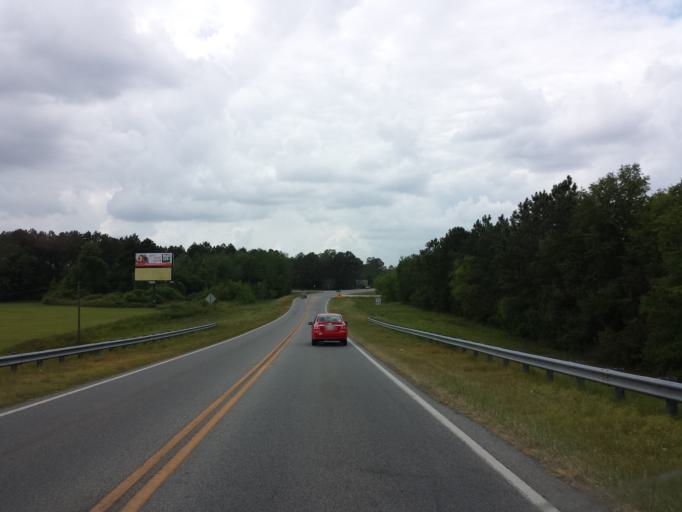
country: US
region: Georgia
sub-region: Cook County
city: Sparks
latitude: 31.1565
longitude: -83.4329
